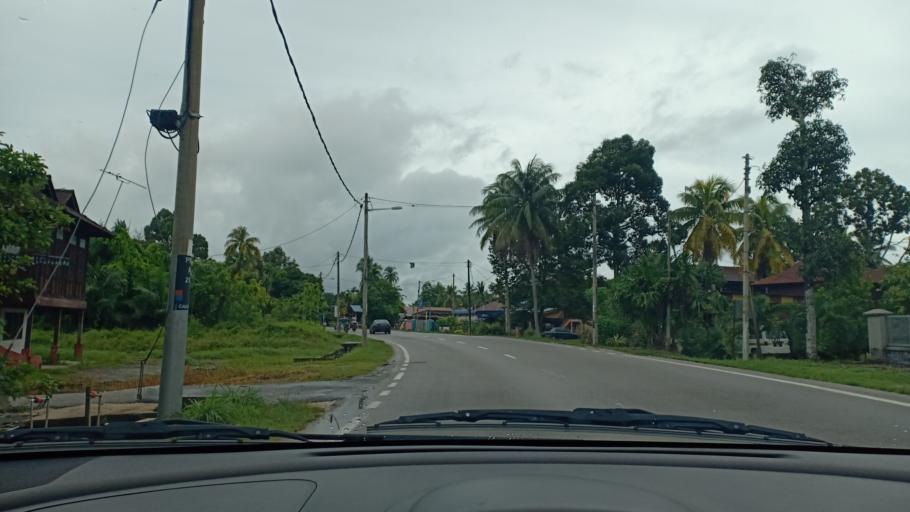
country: MY
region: Penang
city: Kepala Batas
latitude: 5.4965
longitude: 100.4450
